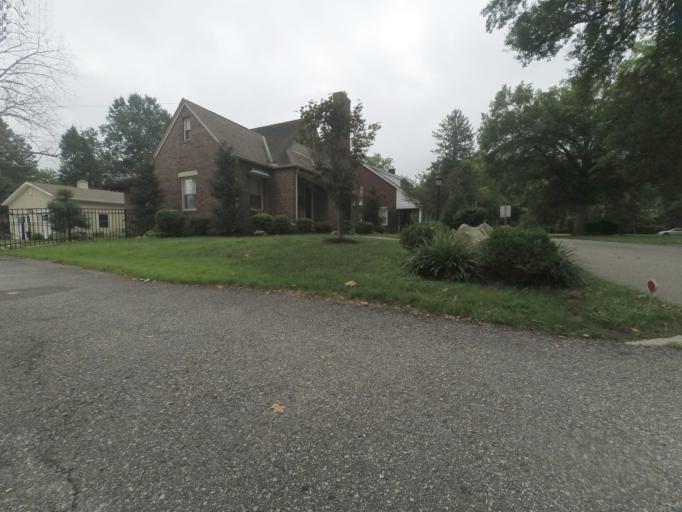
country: US
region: West Virginia
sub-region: Cabell County
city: Huntington
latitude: 38.4049
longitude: -82.4306
